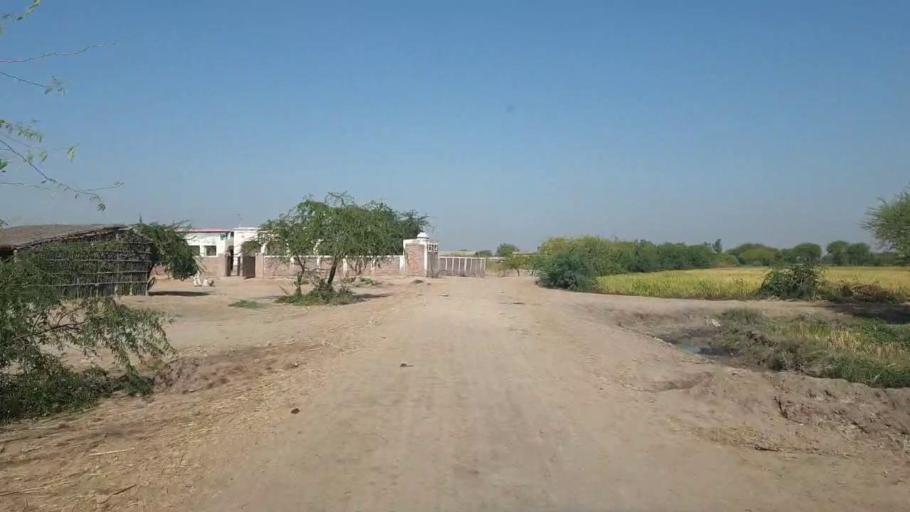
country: PK
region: Sindh
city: Talhar
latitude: 24.8061
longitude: 68.7863
